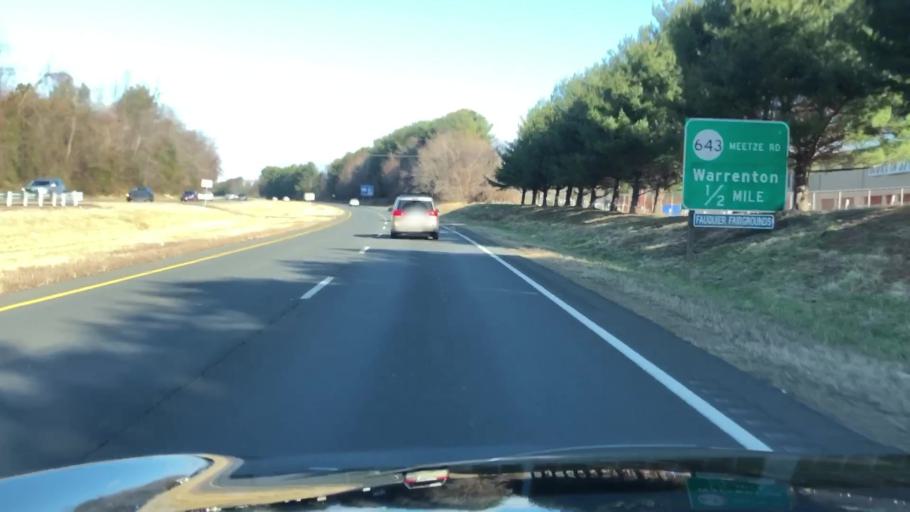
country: US
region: Virginia
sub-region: Fauquier County
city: Warrenton
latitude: 38.6973
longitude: -77.7809
